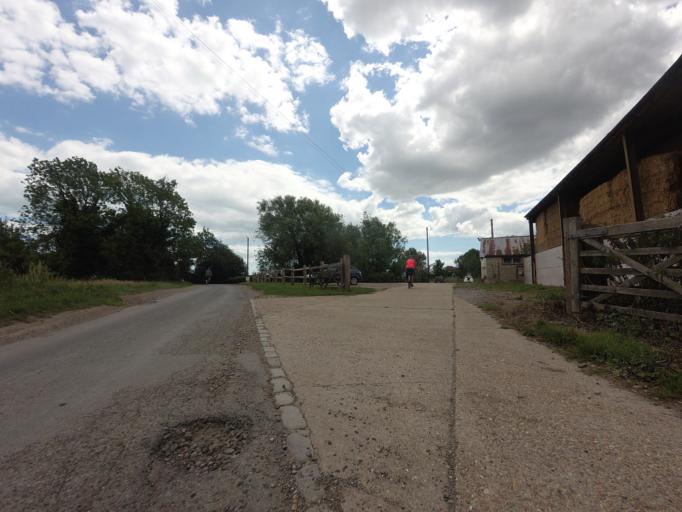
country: GB
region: England
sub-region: East Sussex
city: Pevensey
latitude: 50.8322
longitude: 0.3256
